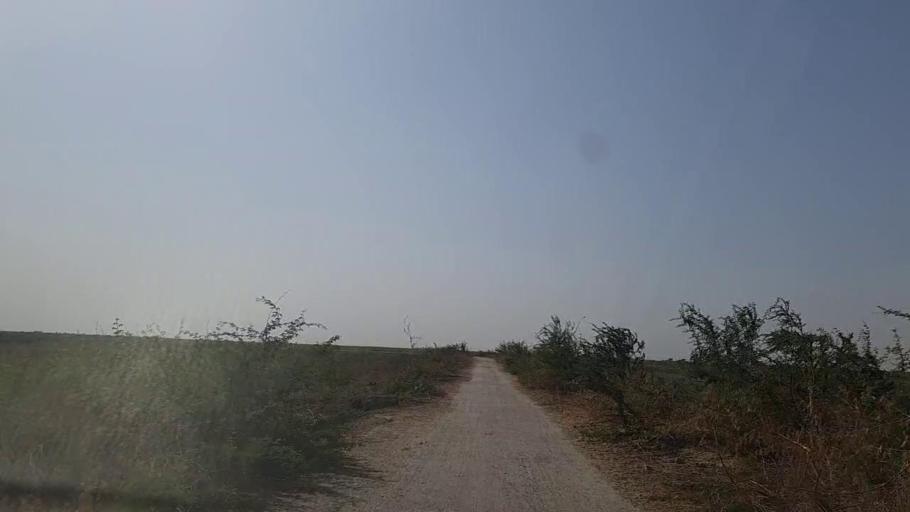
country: PK
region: Sindh
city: Naukot
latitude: 24.5950
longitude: 69.3105
